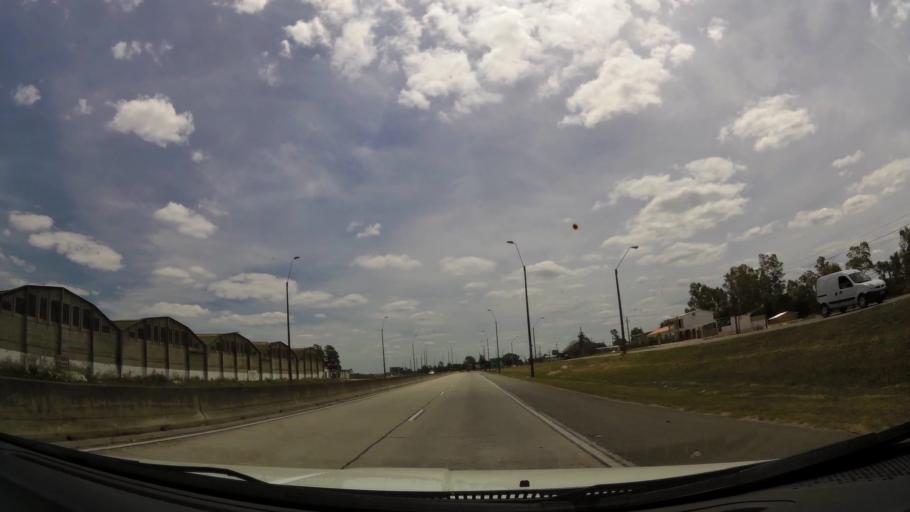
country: UY
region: San Jose
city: Delta del Tigre
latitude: -34.7695
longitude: -56.3889
